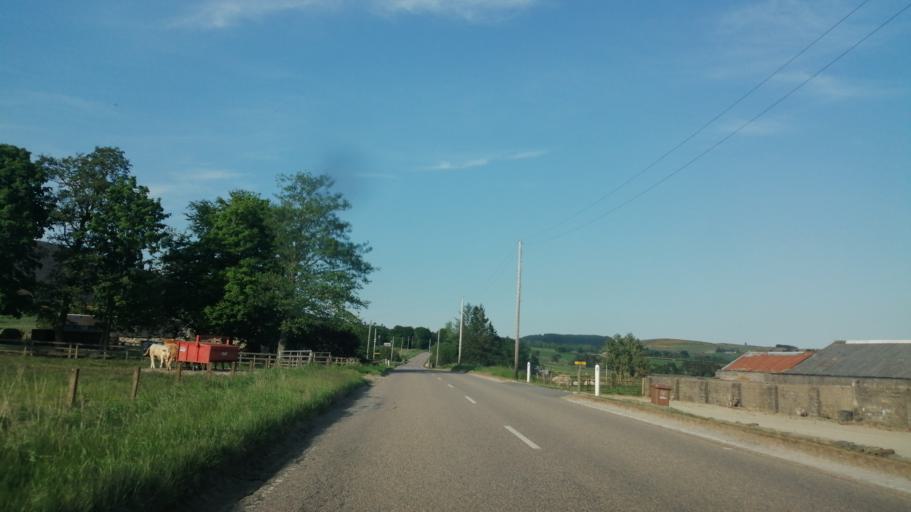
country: GB
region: Scotland
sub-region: Aberdeenshire
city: Huntly
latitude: 57.5650
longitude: -2.7921
